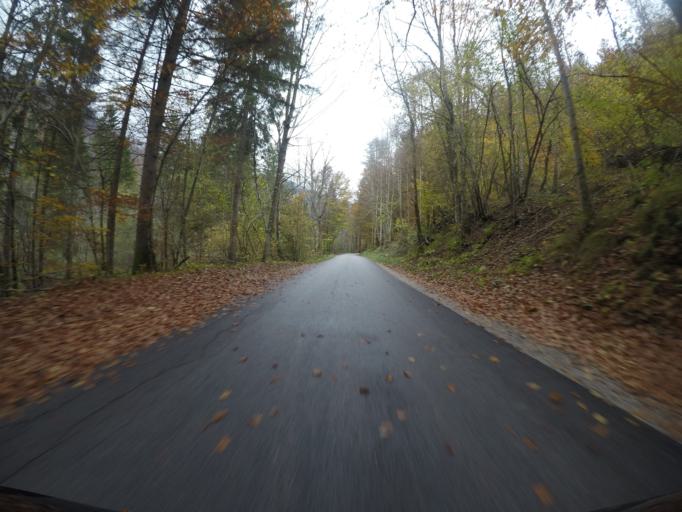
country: SI
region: Jesenice
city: Hrusica
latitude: 46.4195
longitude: 13.9796
